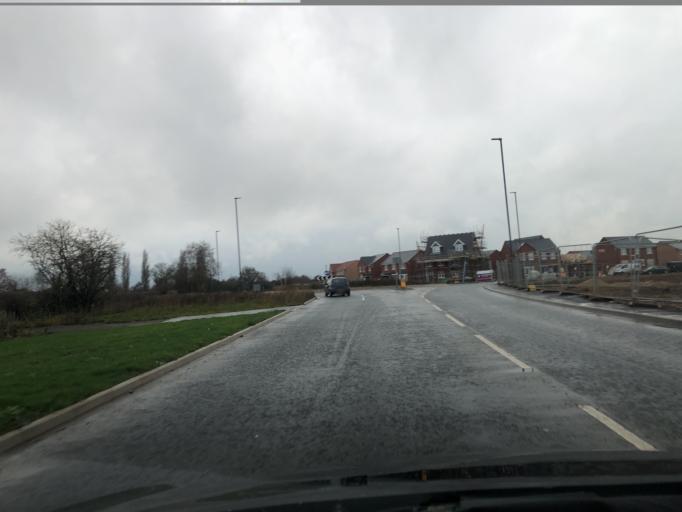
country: GB
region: England
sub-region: North Yorkshire
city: Northallerton
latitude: 54.3520
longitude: -1.4276
